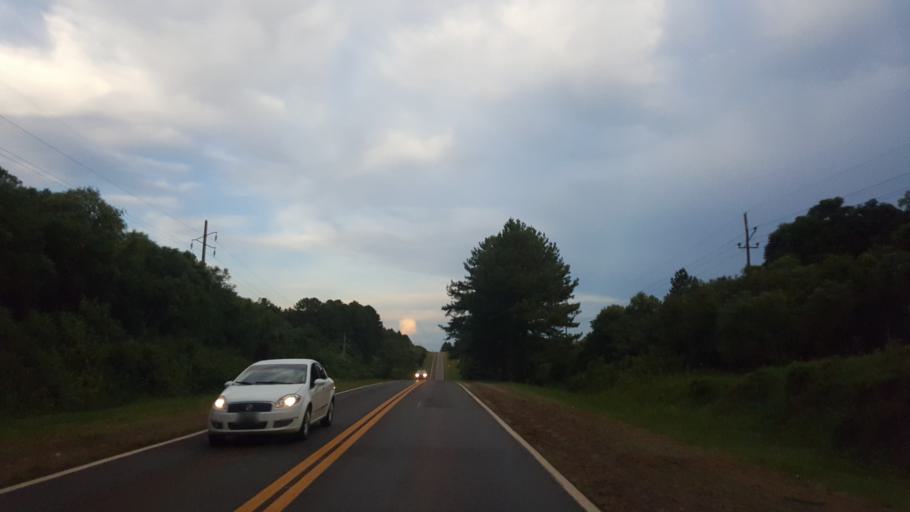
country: AR
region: Misiones
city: Jardin America
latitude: -27.0239
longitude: -55.2062
